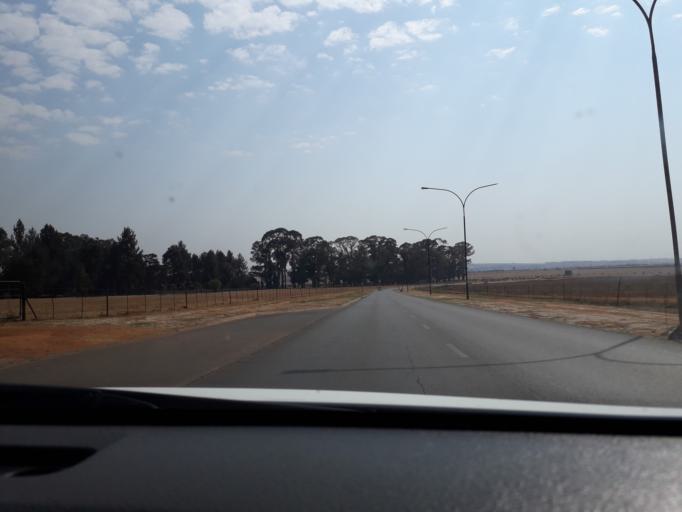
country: ZA
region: Gauteng
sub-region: Ekurhuleni Metropolitan Municipality
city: Tembisa
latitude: -26.0606
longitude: 28.2704
